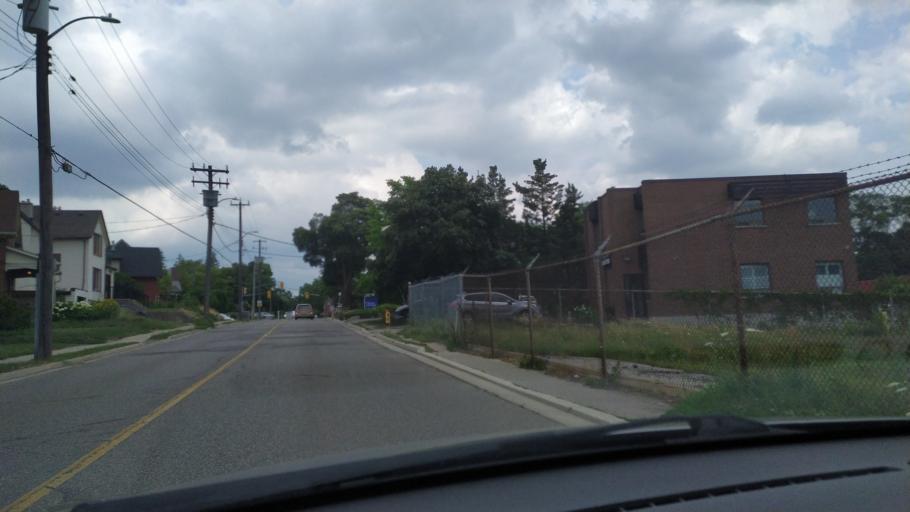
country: CA
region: Ontario
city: Waterloo
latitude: 43.4536
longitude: -80.5120
